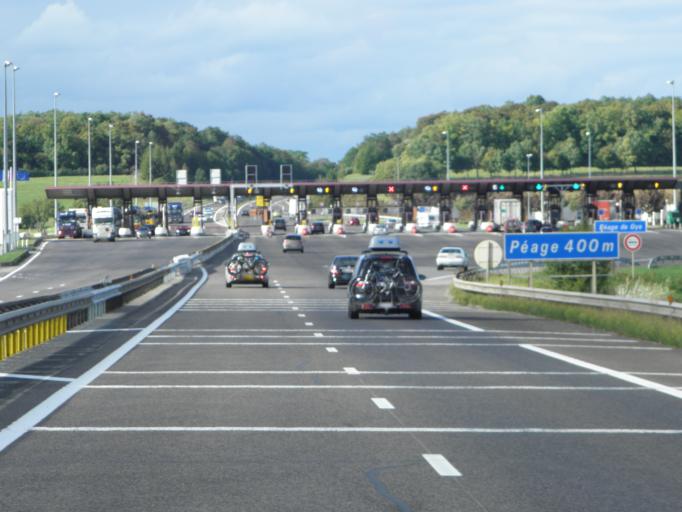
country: FR
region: Lorraine
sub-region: Departement de Meurthe-et-Moselle
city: Dommartin-les-Toul
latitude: 48.6334
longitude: 5.8818
